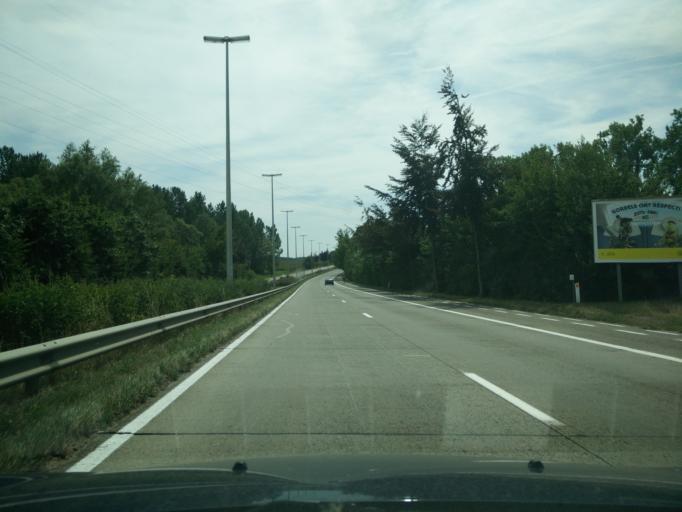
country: BE
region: Flanders
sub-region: Provincie Oost-Vlaanderen
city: Ninove
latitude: 50.8718
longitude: 4.0300
